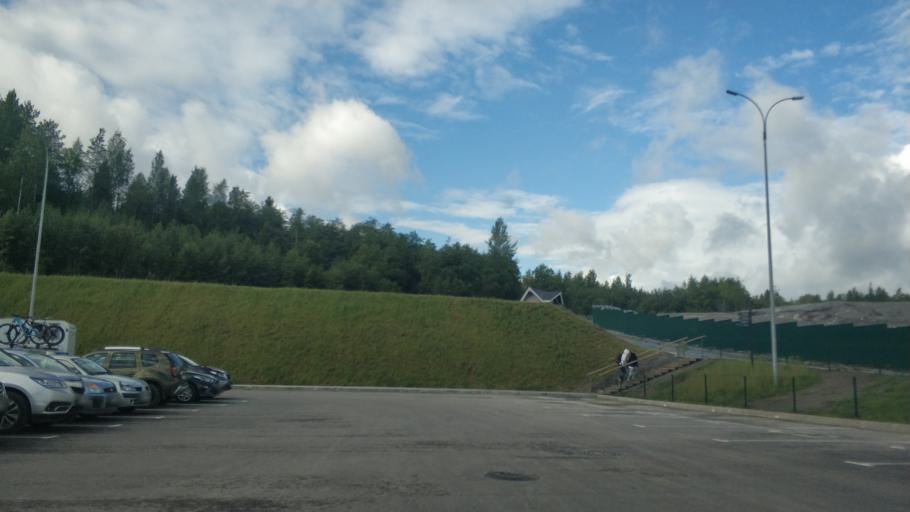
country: RU
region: Republic of Karelia
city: Ruskeala
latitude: 61.9491
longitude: 30.5838
